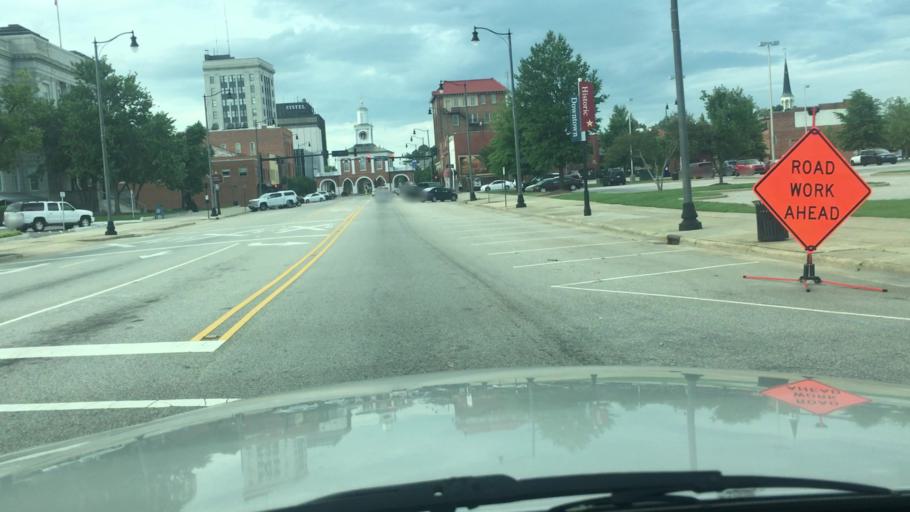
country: US
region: North Carolina
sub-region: Cumberland County
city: Fayetteville
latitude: 35.0506
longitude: -78.8789
